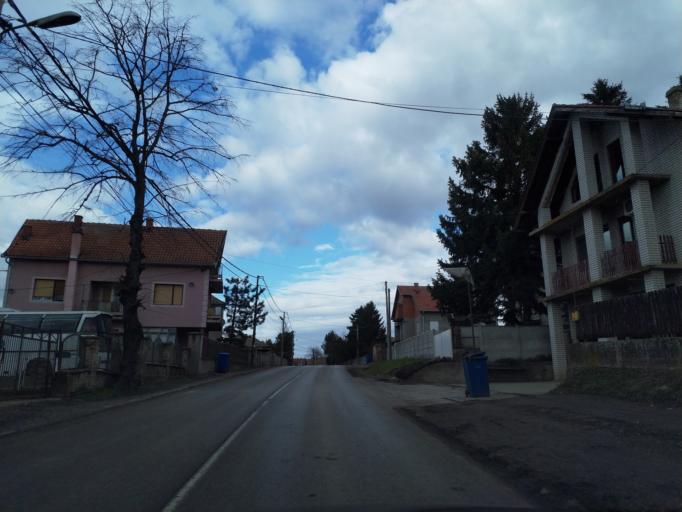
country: RS
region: Central Serbia
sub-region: Belgrade
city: Grocka
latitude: 44.6039
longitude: 20.7257
